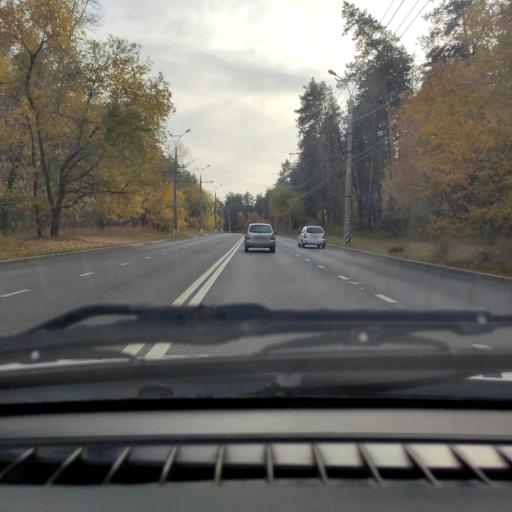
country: RU
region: Samara
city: Zhigulevsk
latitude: 53.4903
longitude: 49.4627
